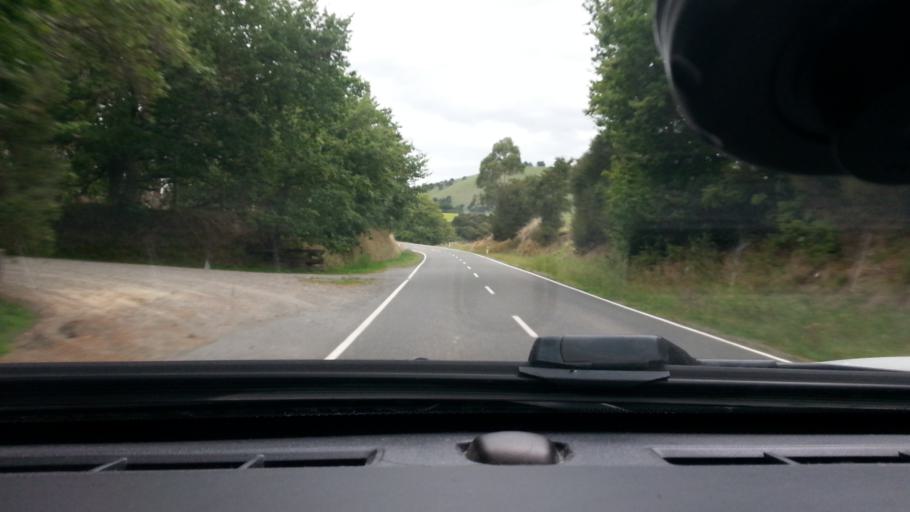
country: NZ
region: Wellington
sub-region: South Wairarapa District
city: Waipawa
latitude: -41.2860
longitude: 175.3246
